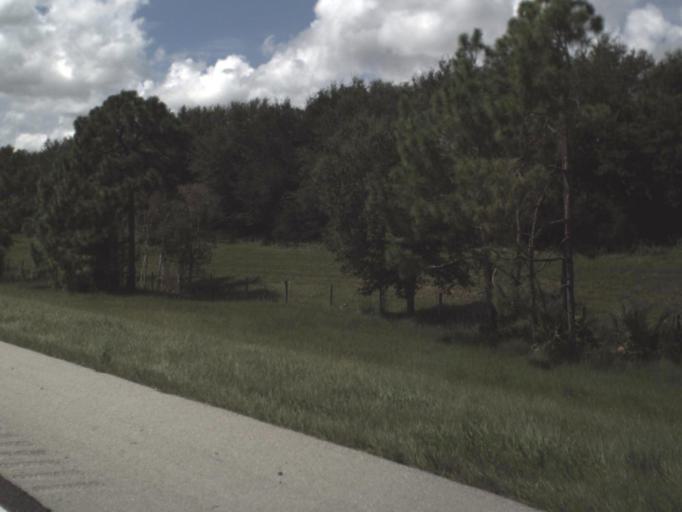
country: US
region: Florida
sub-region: Lee County
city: Gateway
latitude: 26.5568
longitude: -81.7952
